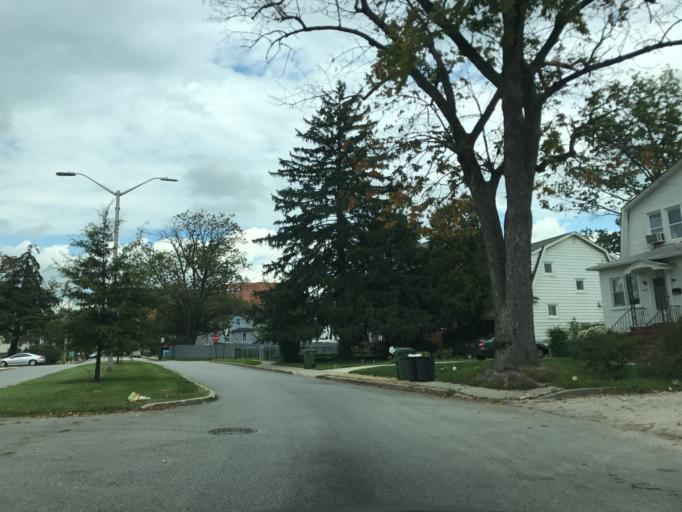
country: US
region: Maryland
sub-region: Baltimore County
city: Lochearn
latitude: 39.3328
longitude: -76.6755
